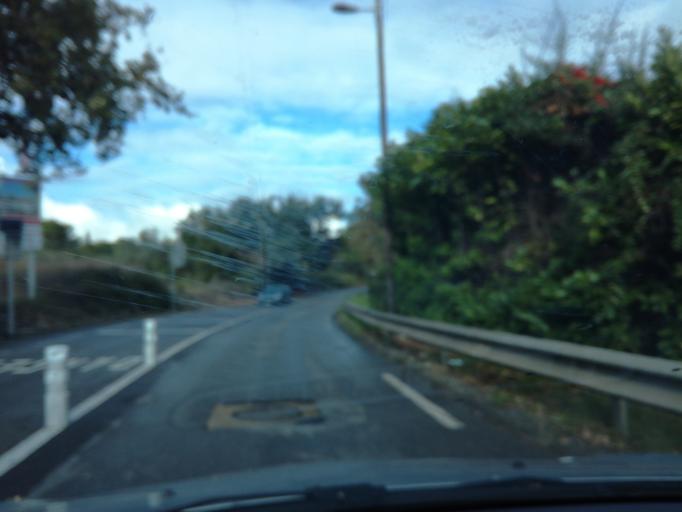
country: FR
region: Provence-Alpes-Cote d'Azur
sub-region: Departement des Alpes-Maritimes
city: Pegomas
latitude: 43.6215
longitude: 6.9351
